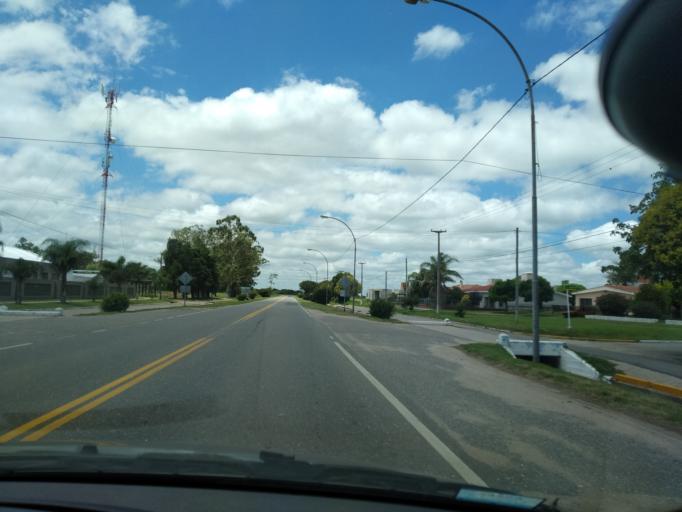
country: AR
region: Cordoba
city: Toledo
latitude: -31.6491
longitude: -64.0861
